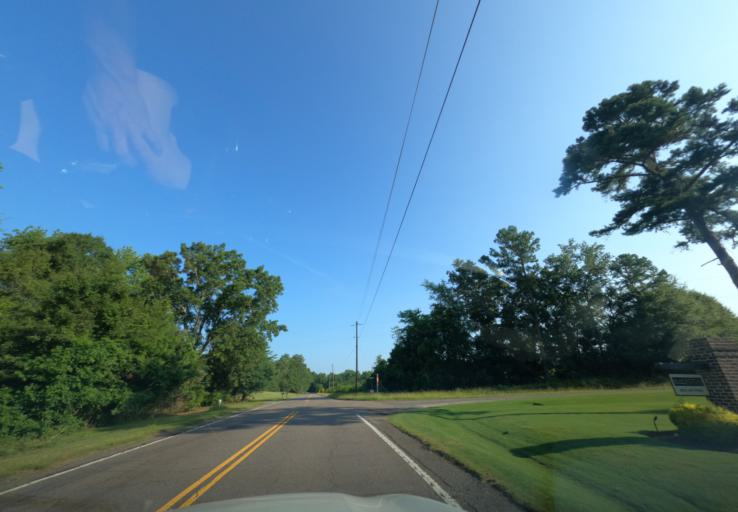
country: US
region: South Carolina
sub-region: Edgefield County
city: Murphys Estates
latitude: 33.6204
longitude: -81.9688
